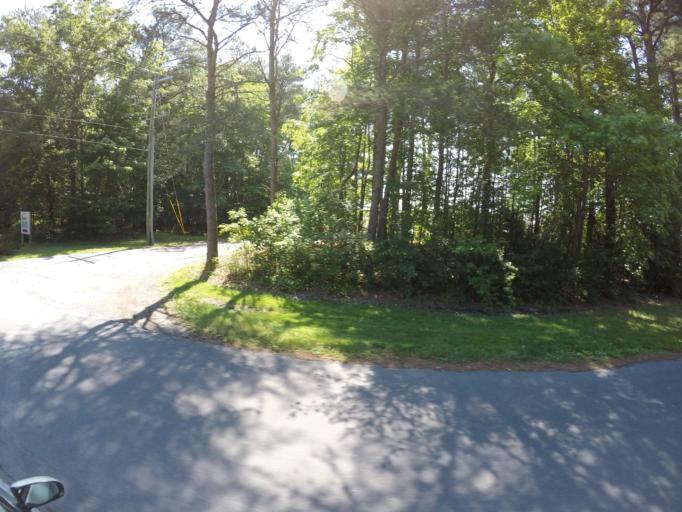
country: US
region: Delaware
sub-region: Sussex County
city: Georgetown
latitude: 38.6943
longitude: -75.3626
